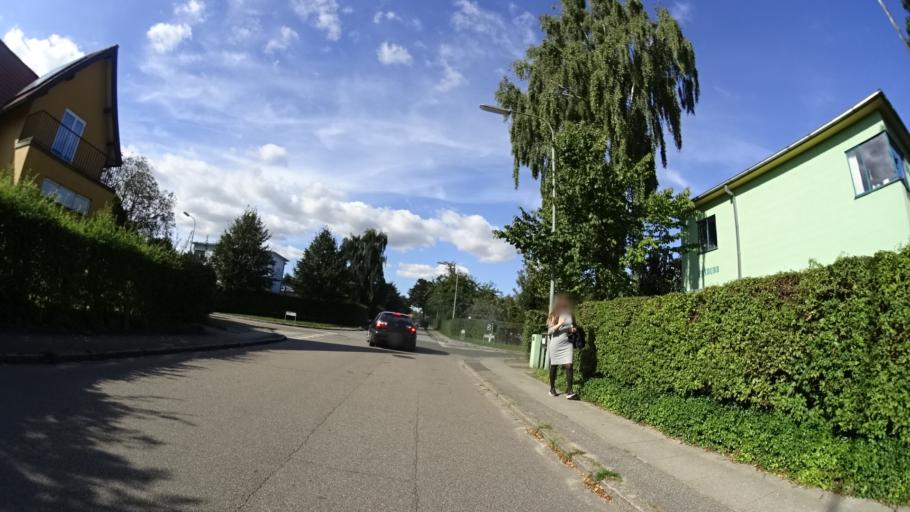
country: DK
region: Central Jutland
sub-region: Arhus Kommune
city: Arhus
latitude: 56.1591
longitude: 10.1686
